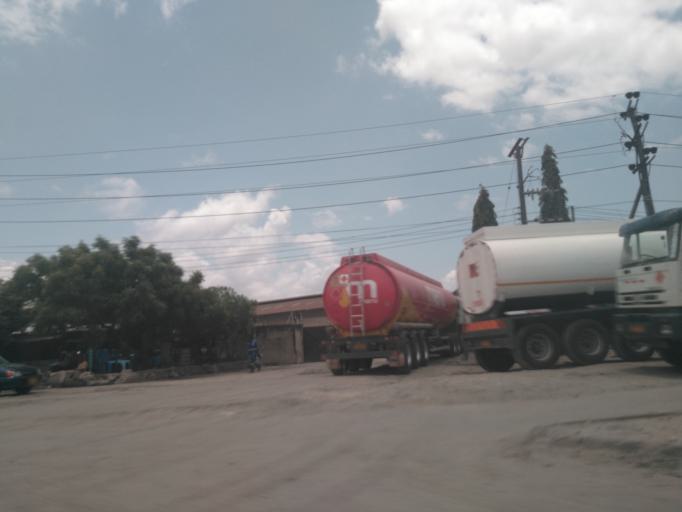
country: TZ
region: Dar es Salaam
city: Dar es Salaam
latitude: -6.8441
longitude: 39.2935
